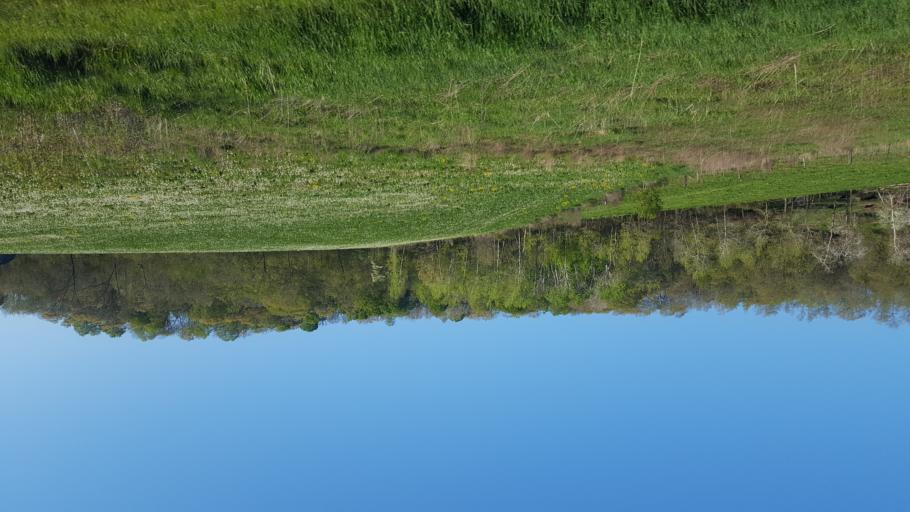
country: US
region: Wisconsin
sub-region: Vernon County
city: Hillsboro
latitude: 43.6105
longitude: -90.3626
